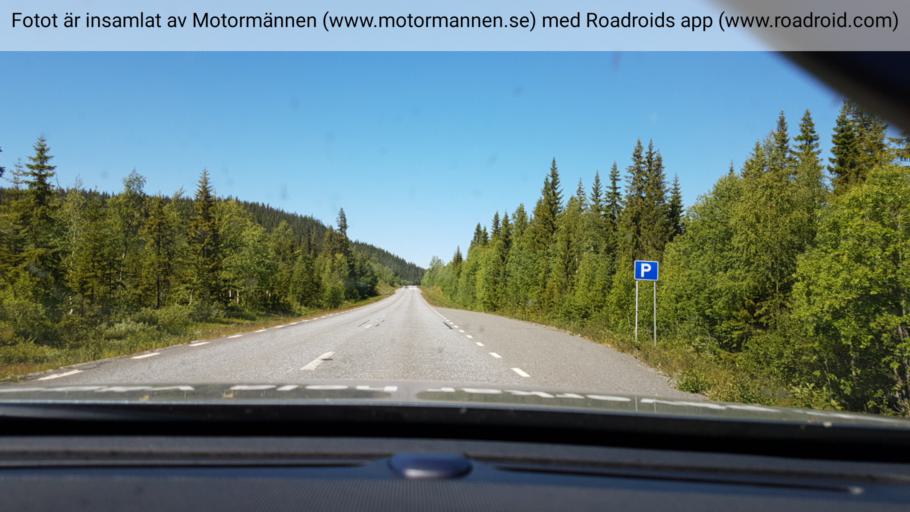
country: SE
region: Vaesterbotten
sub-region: Vilhelmina Kommun
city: Sjoberg
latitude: 64.8749
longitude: 15.8803
